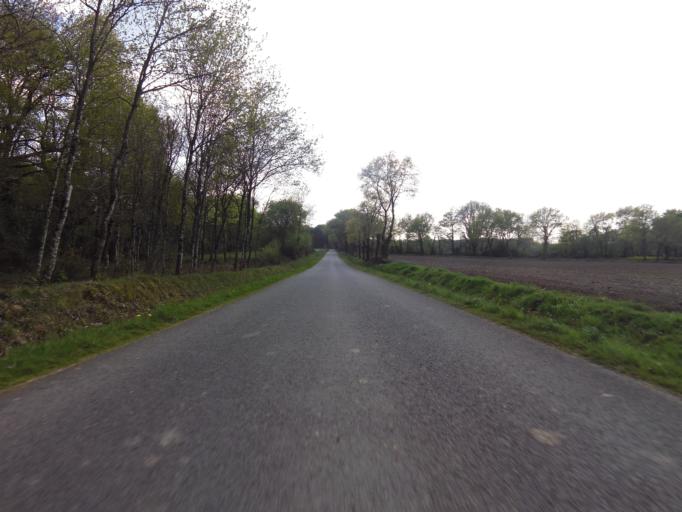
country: FR
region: Brittany
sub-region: Departement du Morbihan
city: Pluherlin
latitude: 47.7272
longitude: -2.3645
